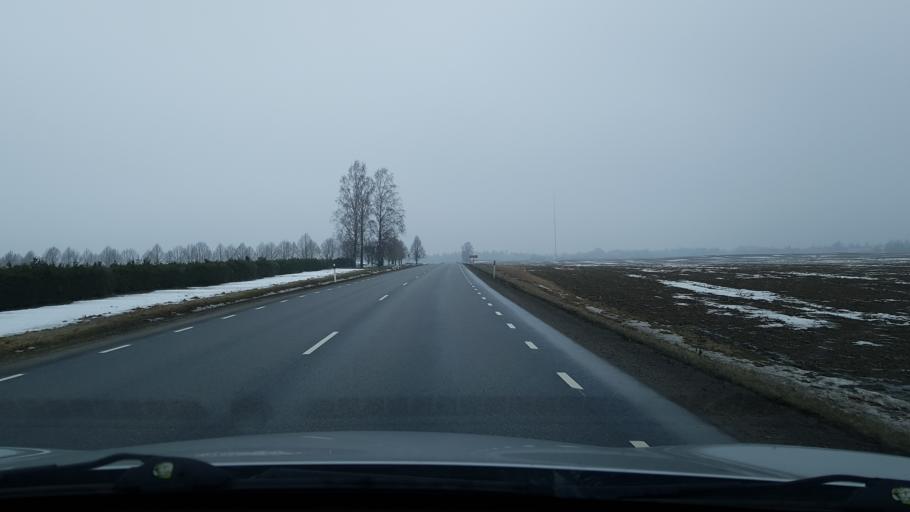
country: EE
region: Viljandimaa
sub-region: Viiratsi vald
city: Viiratsi
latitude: 58.3441
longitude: 25.6269
